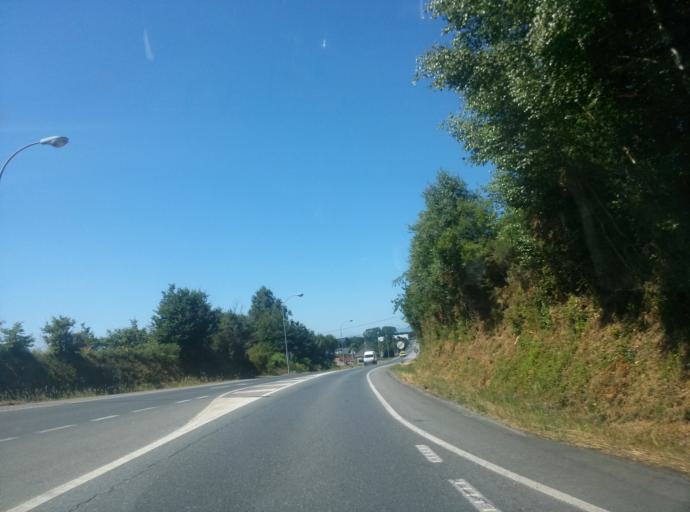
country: ES
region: Galicia
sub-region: Provincia de Lugo
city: Mos
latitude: 43.1271
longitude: -7.4876
